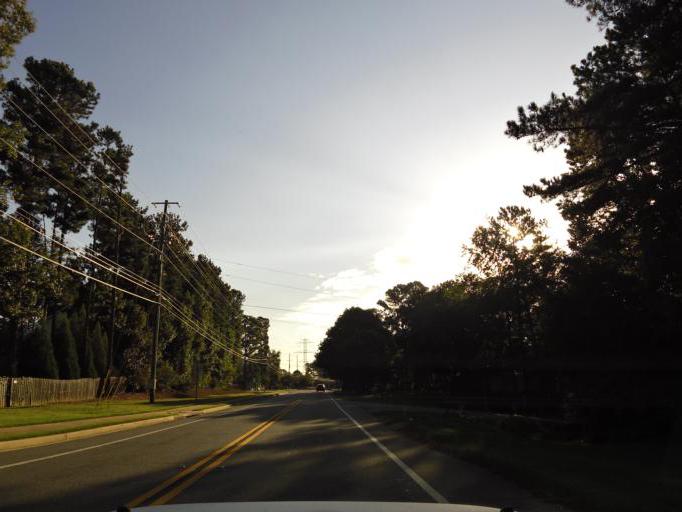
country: US
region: Georgia
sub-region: Cobb County
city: Kennesaw
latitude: 33.9941
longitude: -84.6359
